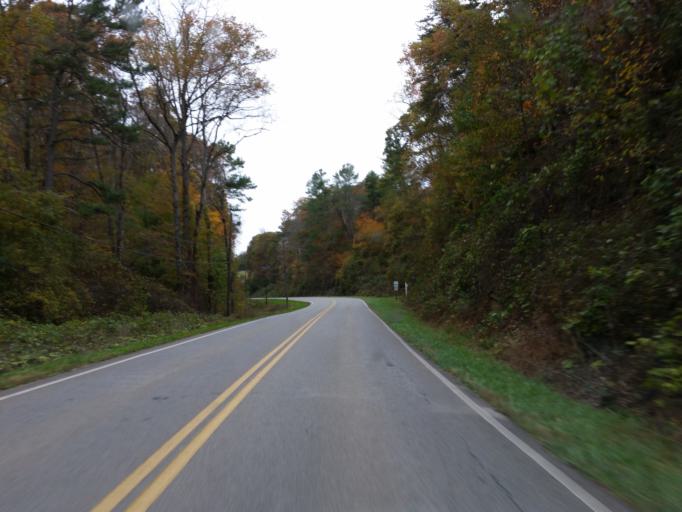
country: US
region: Georgia
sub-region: Pickens County
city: Jasper
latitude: 34.4920
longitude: -84.4262
